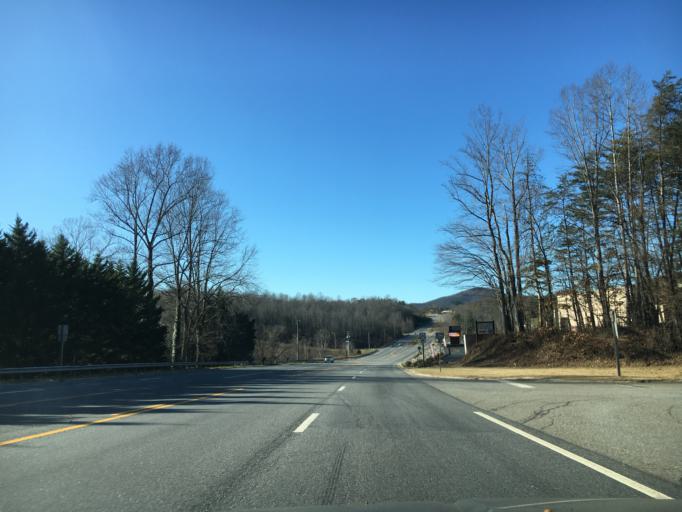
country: US
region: Virginia
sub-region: Patrick County
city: Patrick Springs
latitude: 36.6364
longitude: -80.2125
